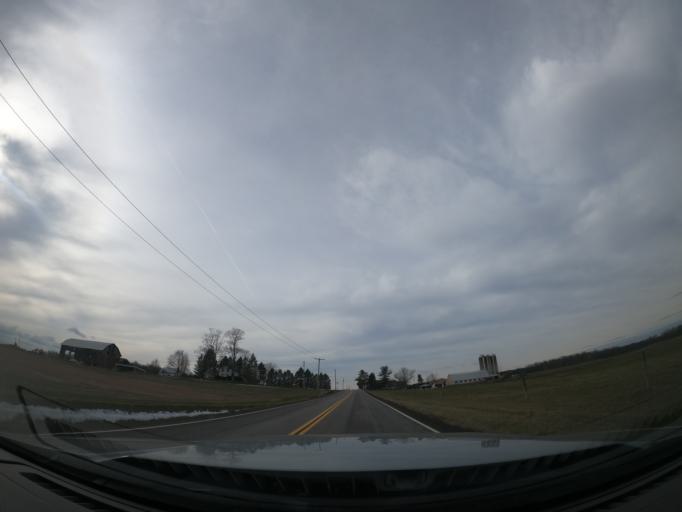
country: US
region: New York
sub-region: Yates County
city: Dundee
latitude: 42.4999
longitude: -76.9402
